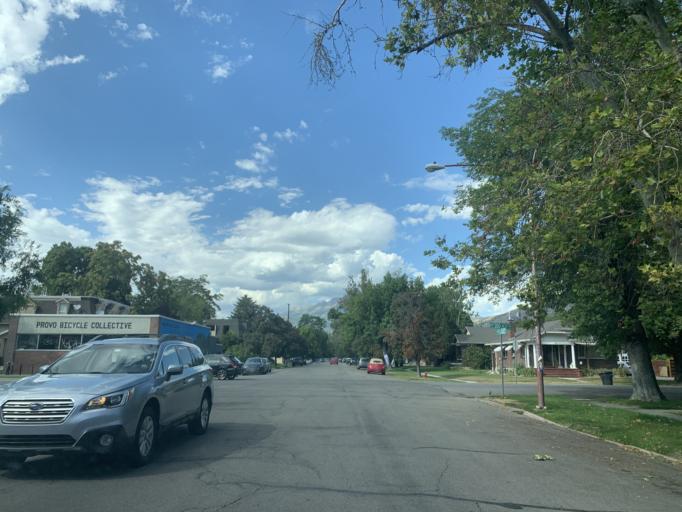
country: US
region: Utah
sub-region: Utah County
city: Provo
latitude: 40.2362
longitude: -111.6517
